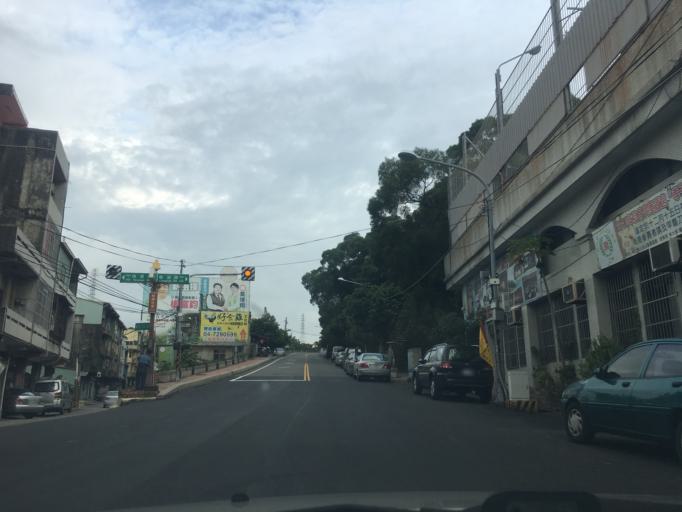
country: TW
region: Taiwan
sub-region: Changhua
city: Chang-hua
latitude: 24.0724
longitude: 120.5612
